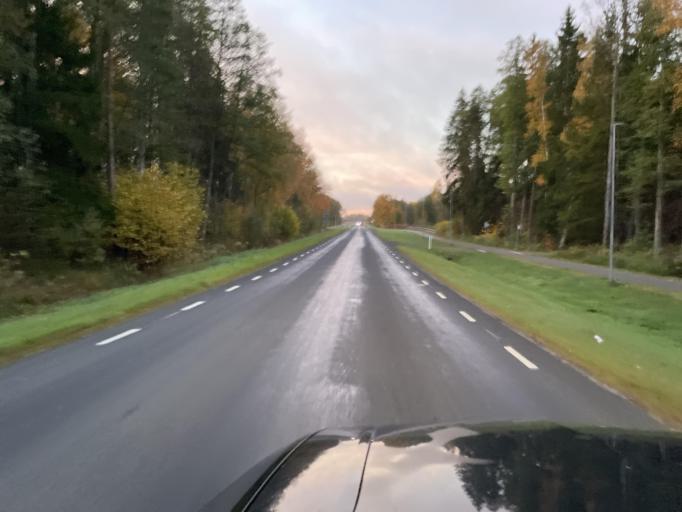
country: EE
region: Harju
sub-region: Nissi vald
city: Riisipere
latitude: 59.2452
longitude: 24.2426
